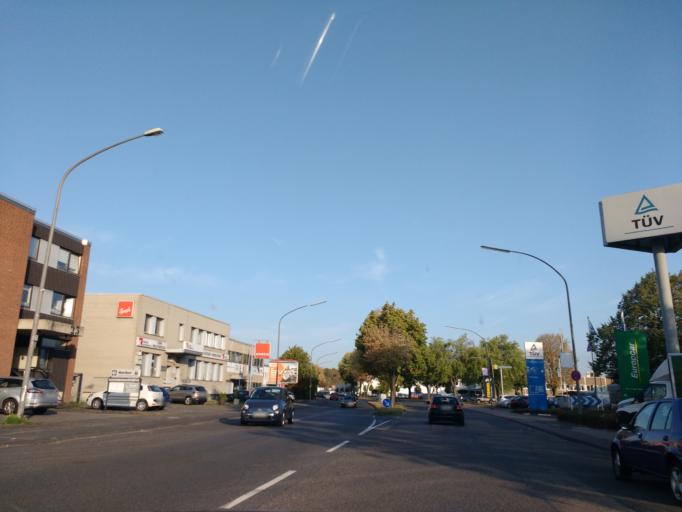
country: DE
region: North Rhine-Westphalia
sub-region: Regierungsbezirk Koln
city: Bilderstoeckchen
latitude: 50.9814
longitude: 6.9174
